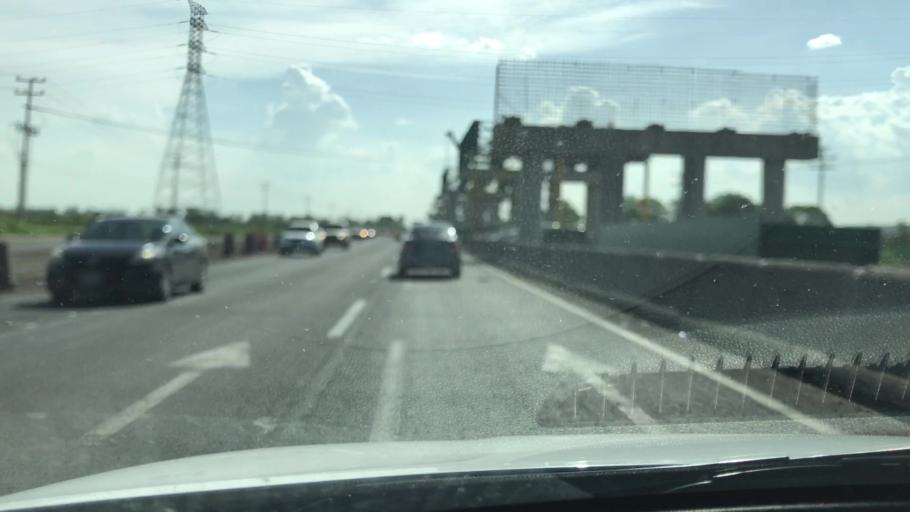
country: MX
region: Guanajuato
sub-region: Celaya
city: Colonia Fraccionamiento el Puente
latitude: 20.5151
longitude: -100.8990
